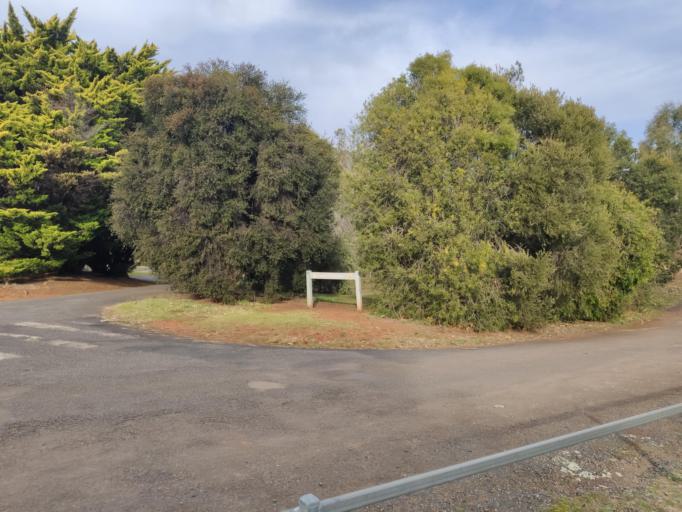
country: AU
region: New South Wales
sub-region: Orange Municipality
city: Orange
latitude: -33.3027
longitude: 149.0301
